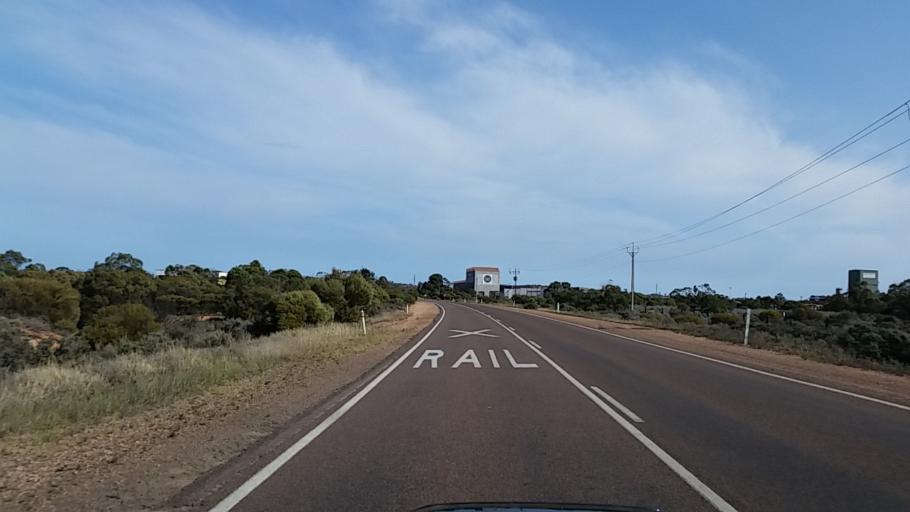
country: AU
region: South Australia
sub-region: Whyalla
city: Whyalla
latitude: -32.9991
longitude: 137.5771
